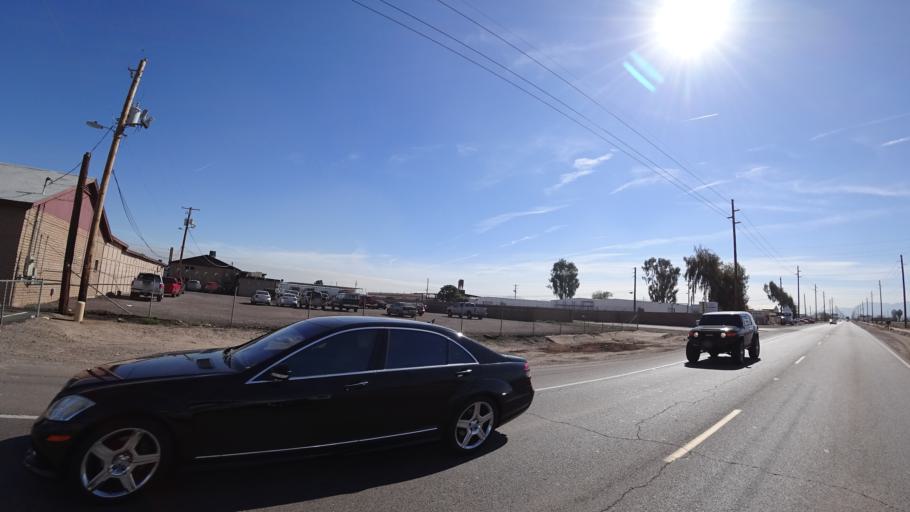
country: US
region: Arizona
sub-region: Maricopa County
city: Laveen
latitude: 33.4341
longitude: -112.1866
